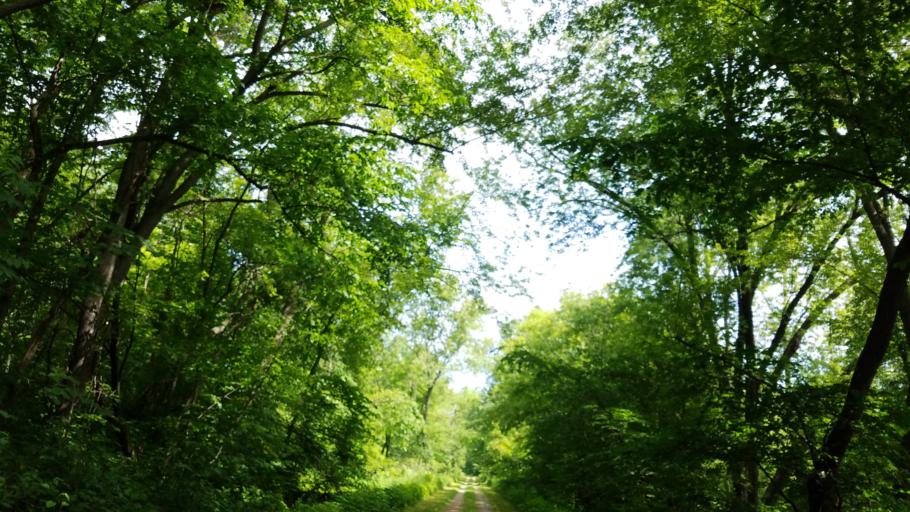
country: US
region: Wisconsin
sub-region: Dunn County
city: Menomonie
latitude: 44.8044
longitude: -91.9470
